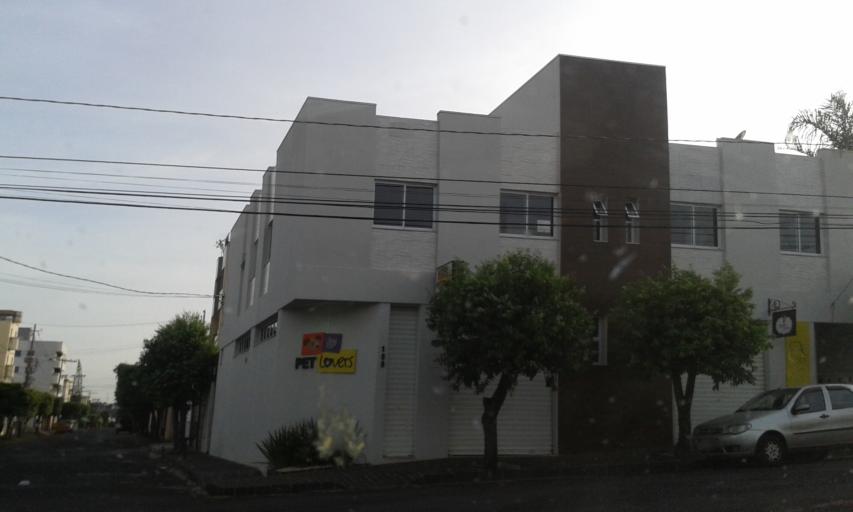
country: BR
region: Minas Gerais
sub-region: Uberlandia
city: Uberlandia
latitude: -18.9213
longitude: -48.2529
